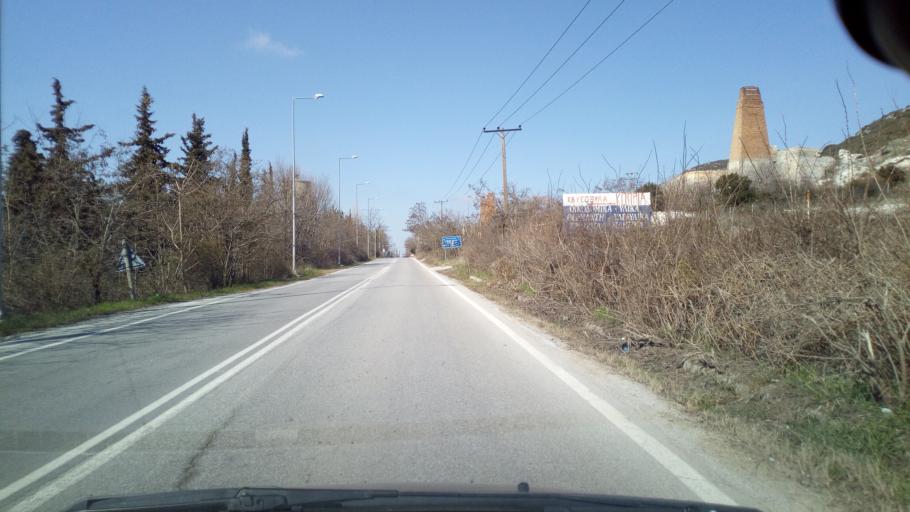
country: GR
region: Central Macedonia
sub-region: Nomos Thessalonikis
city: Chortiatis
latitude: 40.6251
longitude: 23.0690
